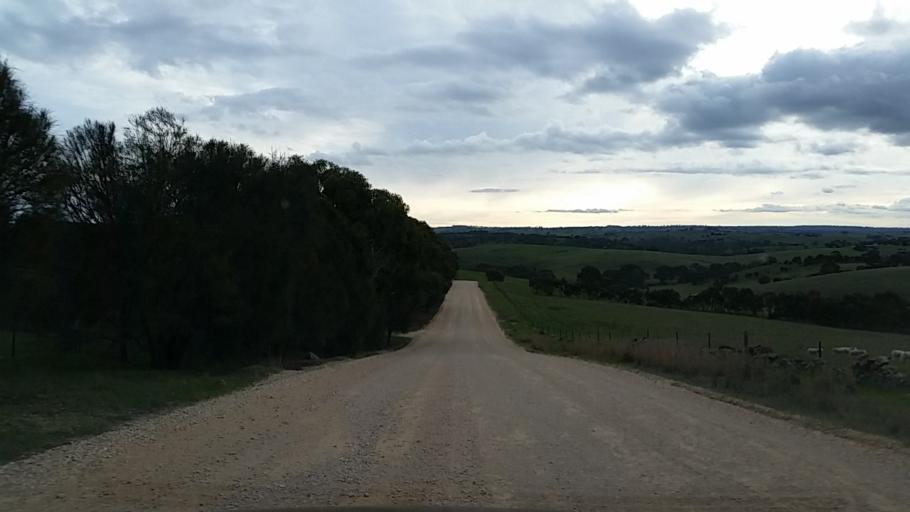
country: AU
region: South Australia
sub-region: Mount Barker
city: Callington
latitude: -34.9984
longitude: 139.0426
